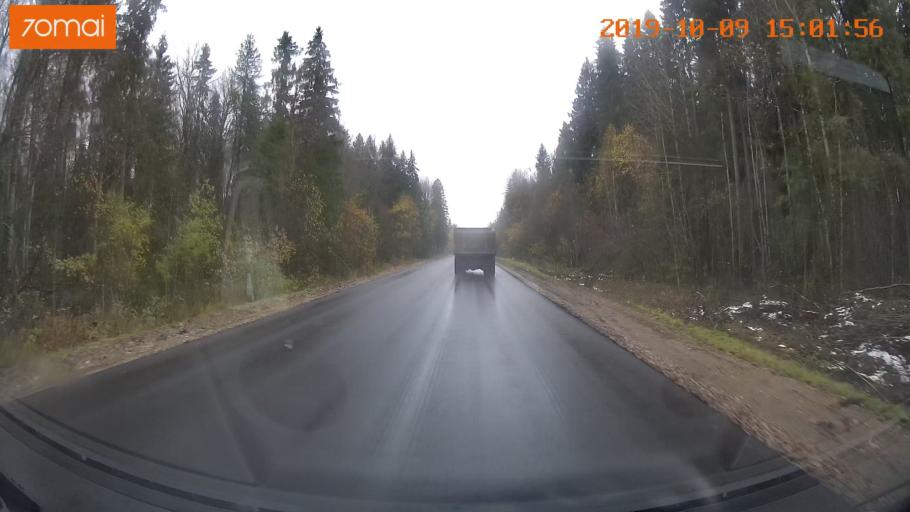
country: RU
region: Kostroma
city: Chistyye Bory
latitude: 58.2914
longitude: 41.6808
